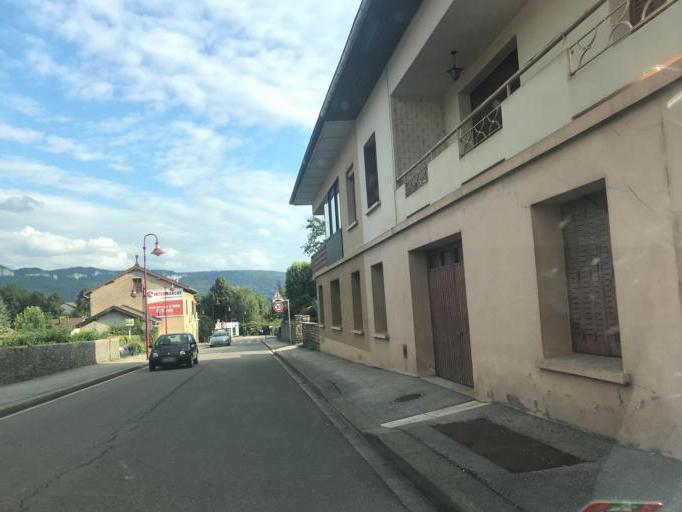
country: FR
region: Franche-Comte
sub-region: Departement du Jura
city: Saint-Lupicin
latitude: 46.3962
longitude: 5.7942
